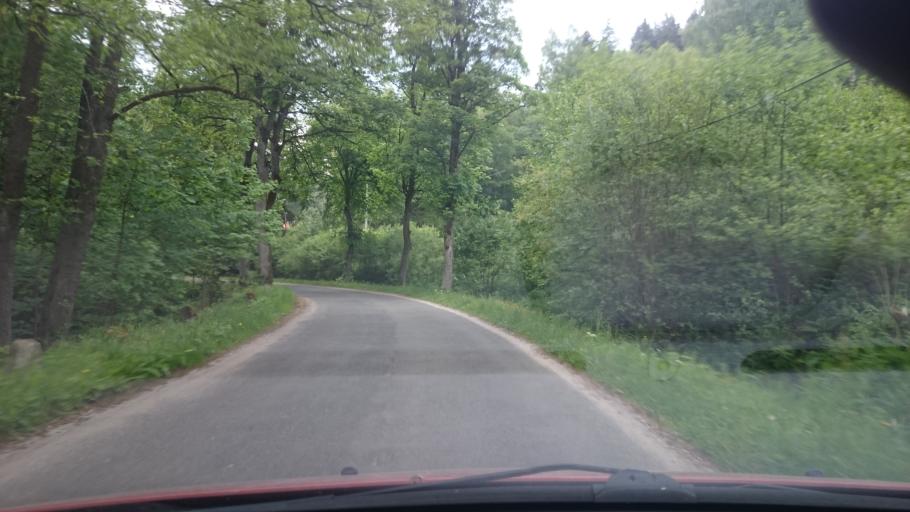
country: PL
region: Lower Silesian Voivodeship
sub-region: Powiat klodzki
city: Polanica-Zdroj
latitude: 50.3043
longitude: 16.5262
